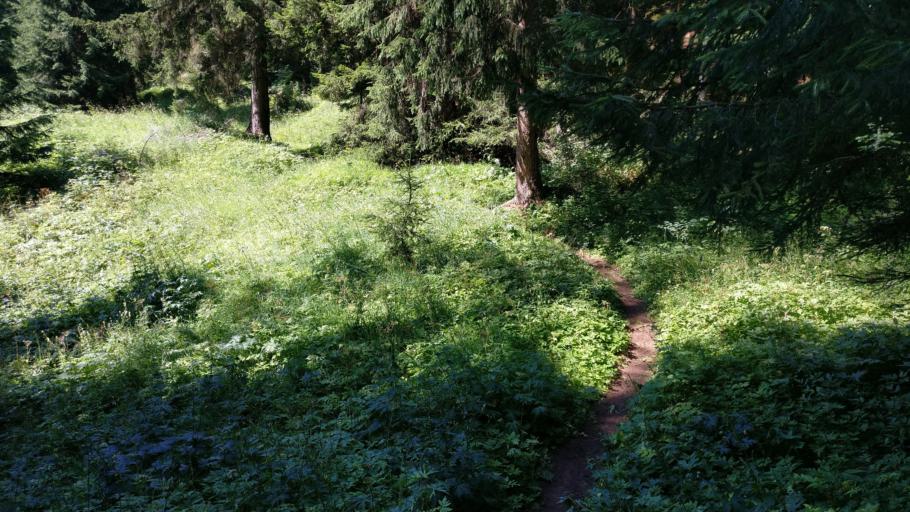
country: IT
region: Trentino-Alto Adige
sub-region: Provincia di Trento
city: Ruffre
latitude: 46.4332
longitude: 11.1901
